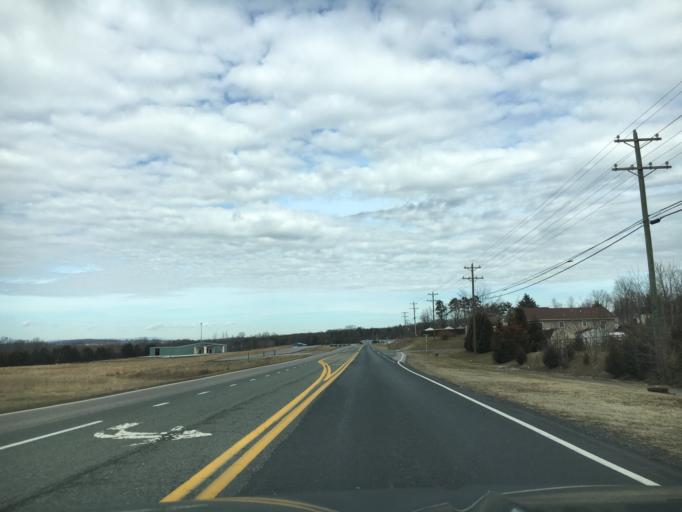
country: US
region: Virginia
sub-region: Augusta County
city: Crimora
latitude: 38.1354
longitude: -78.8453
